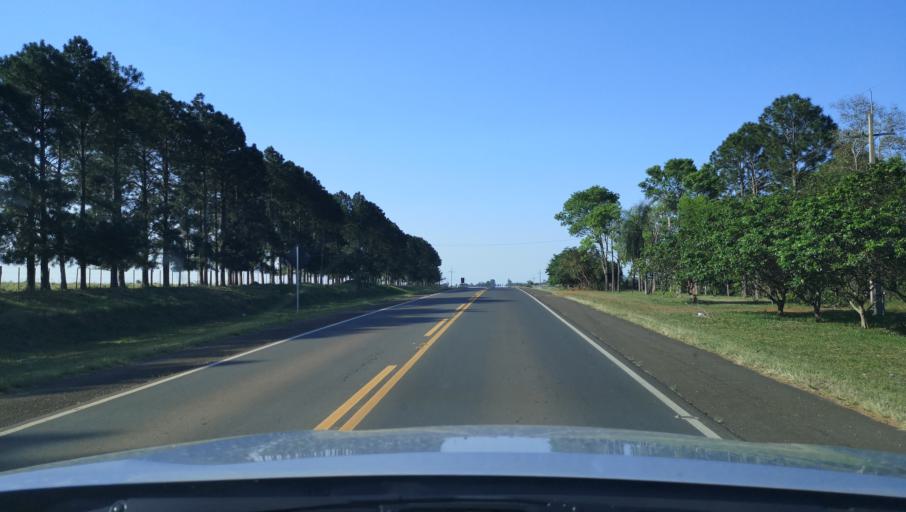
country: PY
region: Misiones
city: Santa Maria
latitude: -26.8418
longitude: -57.0366
